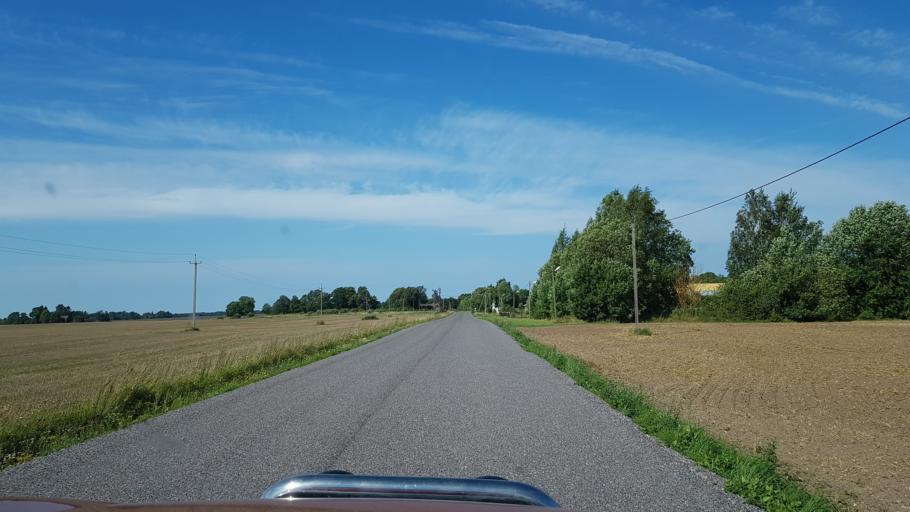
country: EE
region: Tartu
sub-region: Puhja vald
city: Puhja
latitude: 58.2593
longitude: 26.3095
